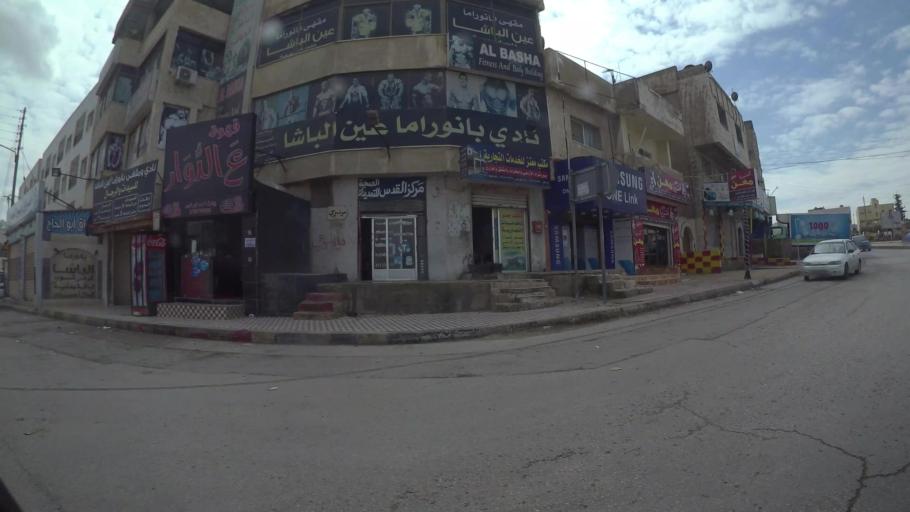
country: JO
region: Amman
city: Al Jubayhah
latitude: 32.0628
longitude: 35.8366
